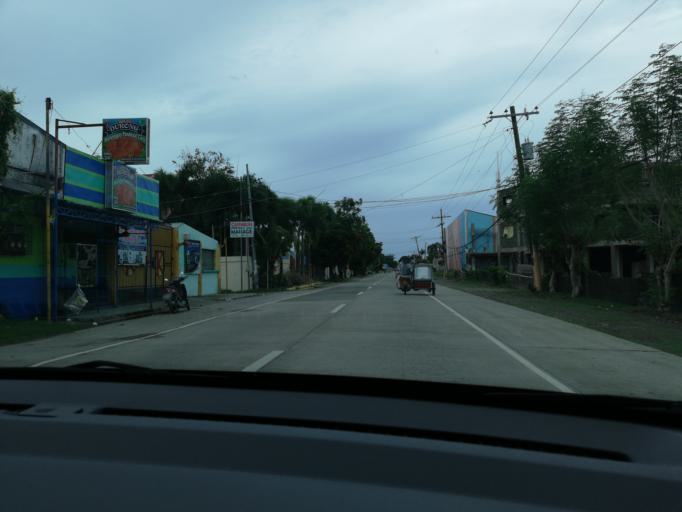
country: PH
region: Ilocos
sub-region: Province of Ilocos Sur
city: Bantay
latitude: 17.5837
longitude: 120.3790
